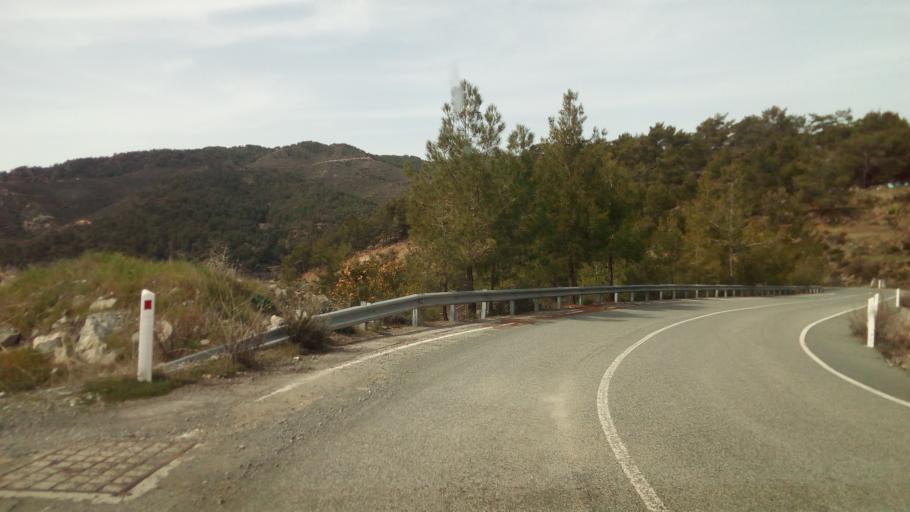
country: CY
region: Limassol
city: Pelendri
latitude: 34.9016
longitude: 32.9959
